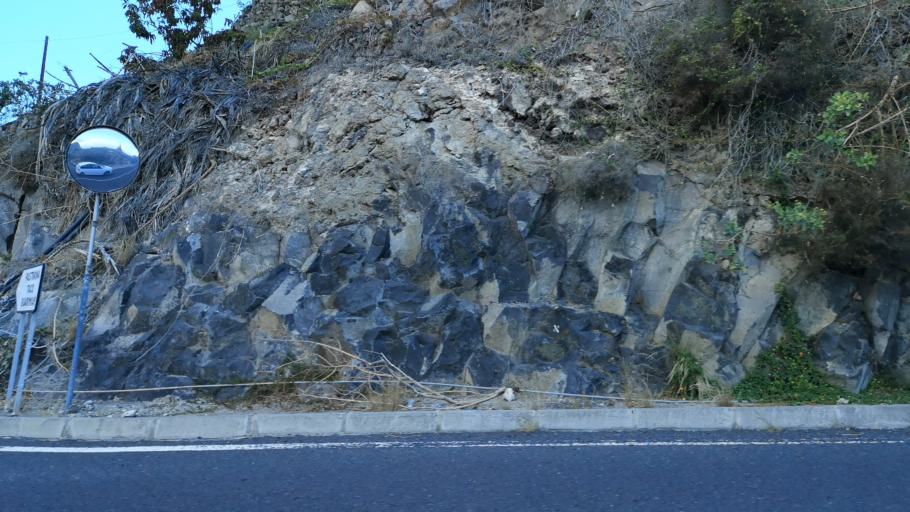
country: ES
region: Canary Islands
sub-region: Provincia de Santa Cruz de Tenerife
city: Alajero
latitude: 28.0347
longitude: -17.1963
